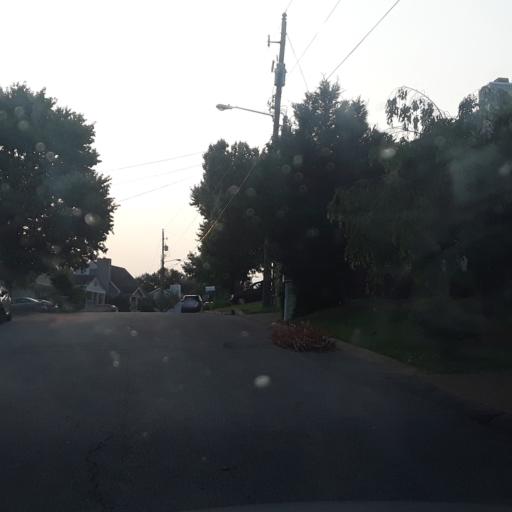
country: US
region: Tennessee
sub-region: Williamson County
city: Brentwood Estates
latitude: 36.0458
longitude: -86.7337
